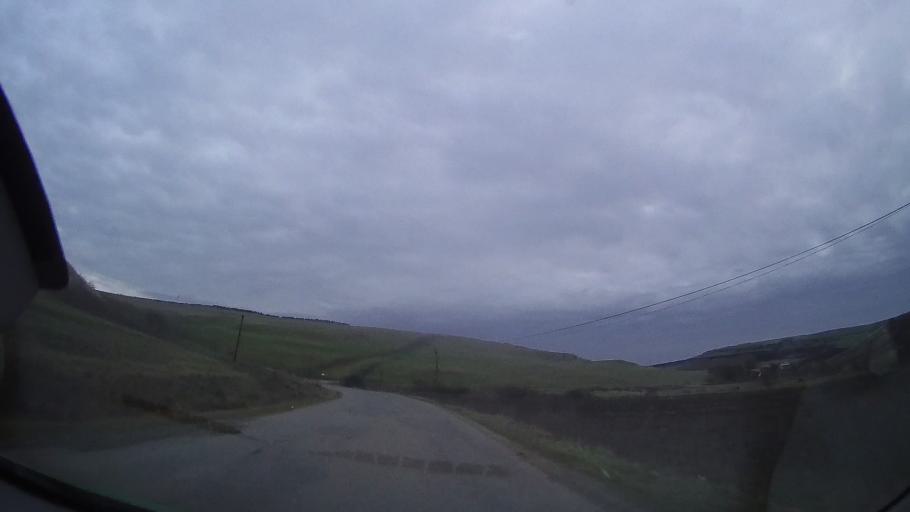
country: RO
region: Cluj
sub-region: Comuna Caianu
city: Vaida-Camaras
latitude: 46.8173
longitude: 23.9352
